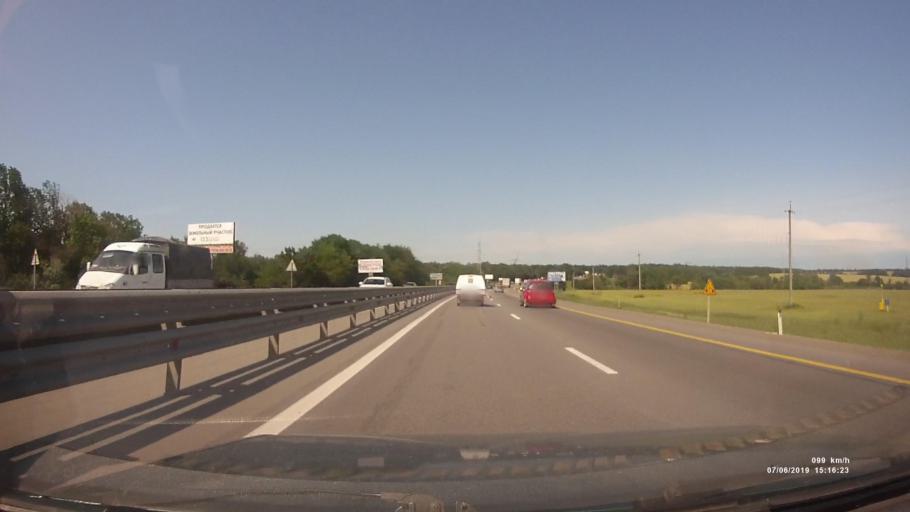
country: RU
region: Rostov
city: Grushevskaya
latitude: 47.3922
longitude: 39.9177
